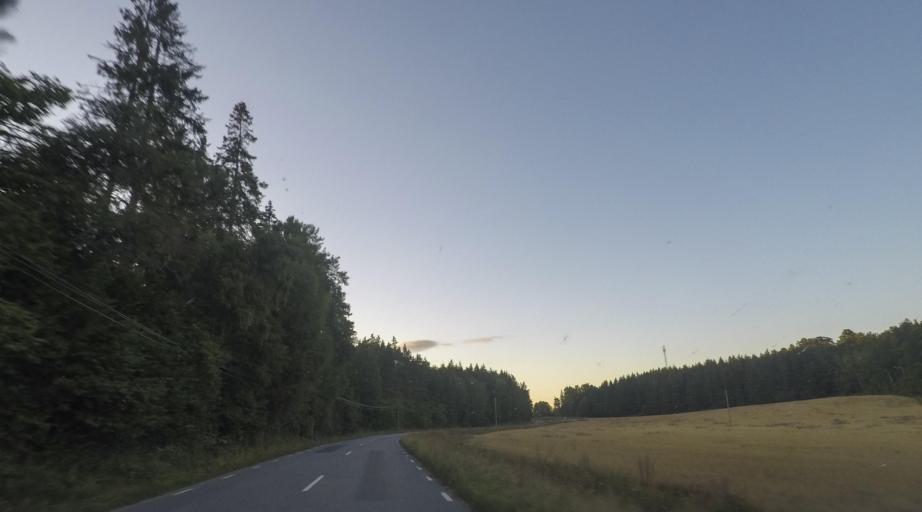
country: SE
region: Soedermanland
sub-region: Trosa Kommun
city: Trosa
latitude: 58.9697
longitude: 17.6937
